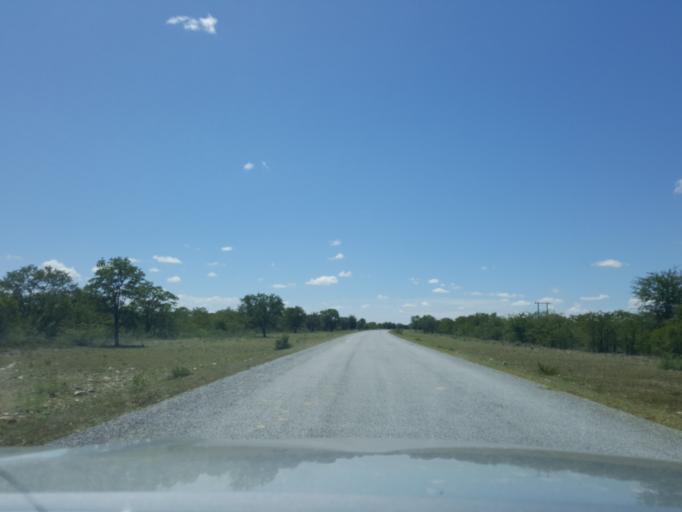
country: BW
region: Central
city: Gweta
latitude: -20.1674
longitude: 25.4008
